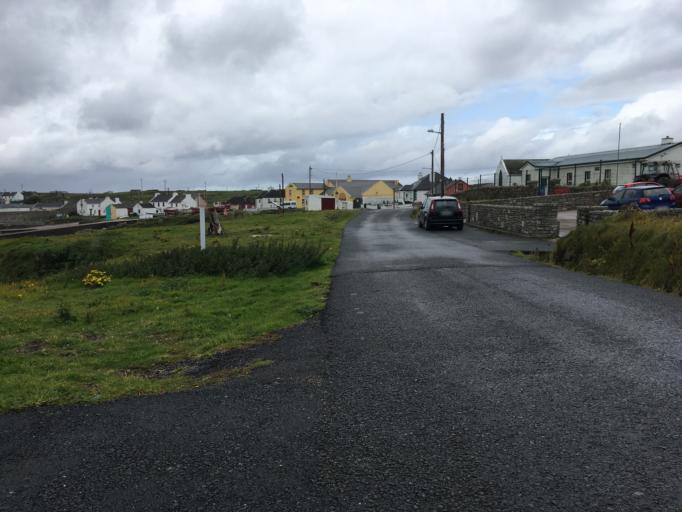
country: IE
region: Ulster
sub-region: County Donegal
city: Derrybeg
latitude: 55.2645
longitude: -8.2239
